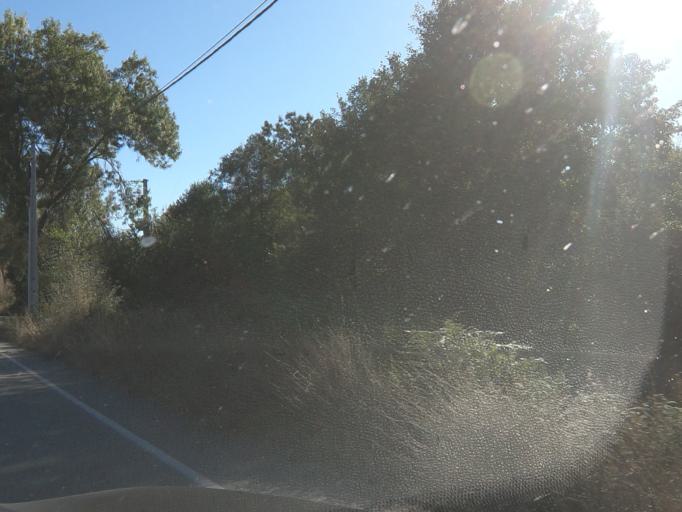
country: PT
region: Vila Real
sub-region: Valpacos
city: Valpacos
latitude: 41.6485
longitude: -7.3209
